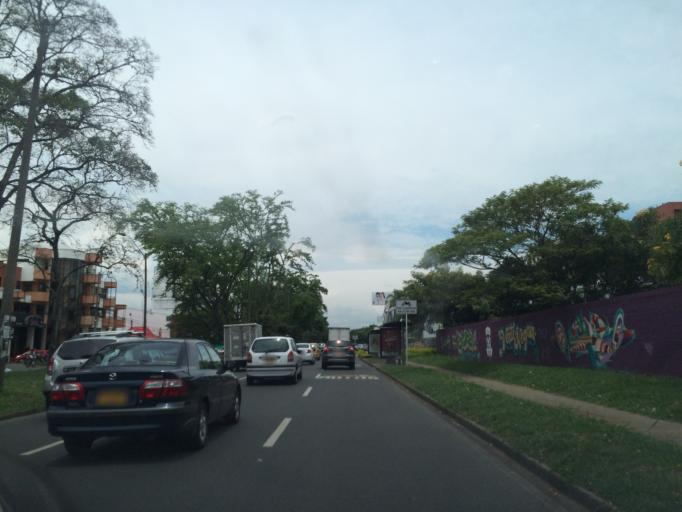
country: CO
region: Valle del Cauca
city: Cali
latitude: 3.3947
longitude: -76.5380
